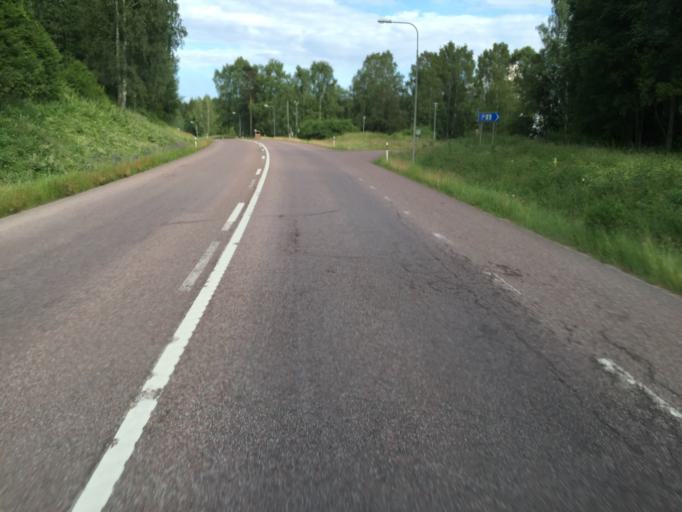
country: SE
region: Dalarna
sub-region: Borlange Kommun
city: Borlaenge
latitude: 60.5306
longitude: 15.3127
